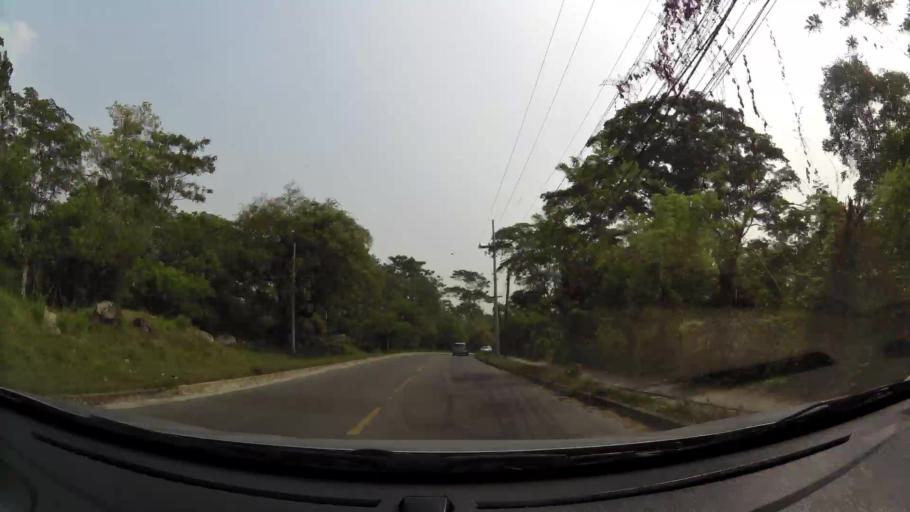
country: HN
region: Cortes
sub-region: San Pedro Sula
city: Pena Blanca
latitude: 15.5628
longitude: -88.0308
